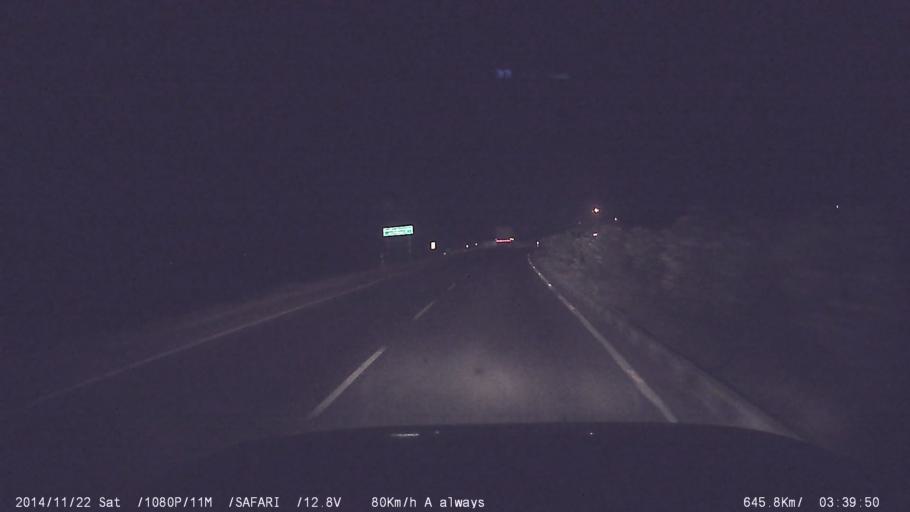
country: IN
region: Tamil Nadu
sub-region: Namakkal
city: Tiruchengode
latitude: 11.4604
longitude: 77.8207
